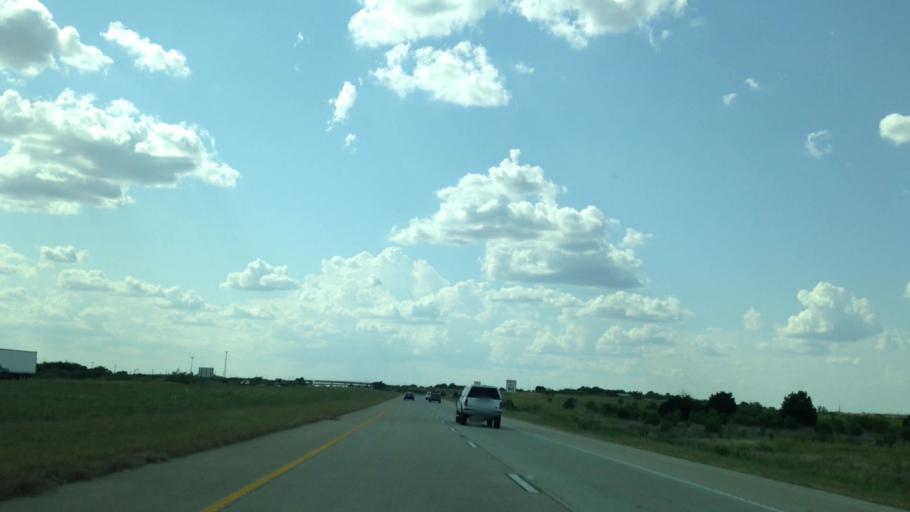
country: US
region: Texas
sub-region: Travis County
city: Onion Creek
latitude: 30.0878
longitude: -97.7437
